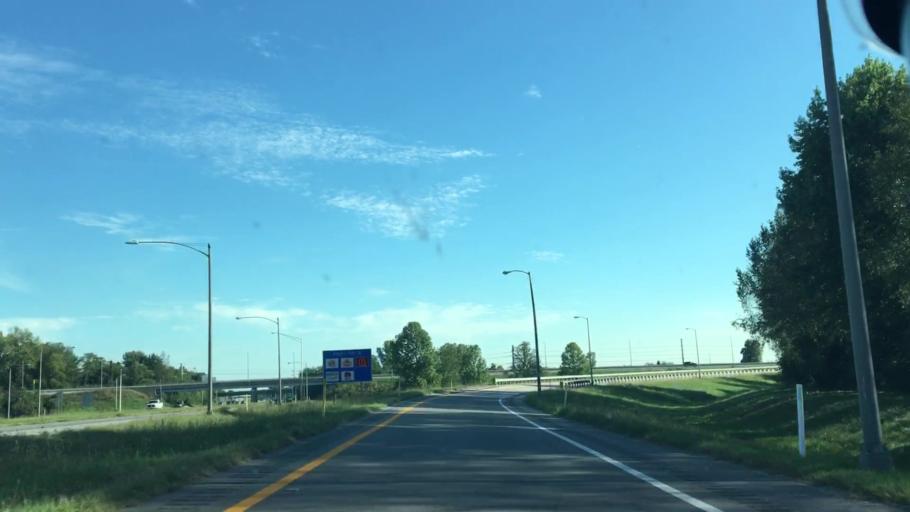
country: US
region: Kentucky
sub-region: Daviess County
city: Owensboro
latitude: 37.7681
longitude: -87.1647
